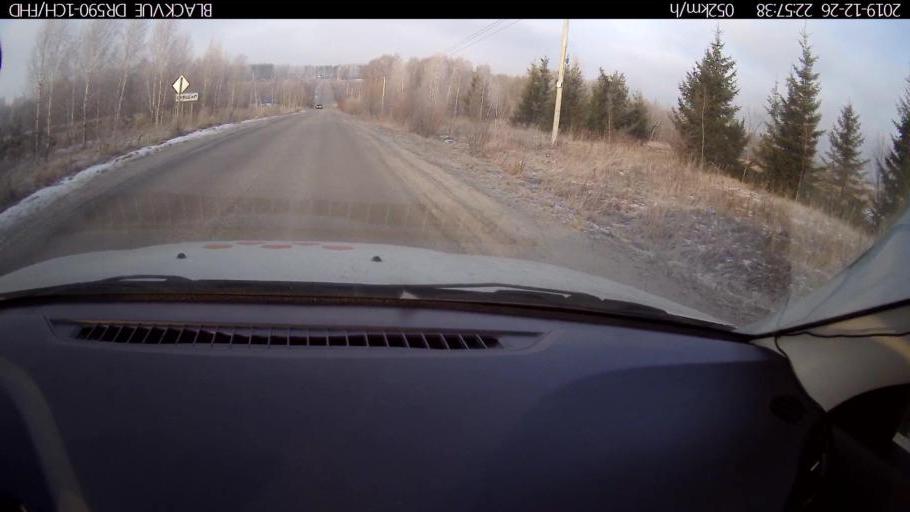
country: RU
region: Nizjnij Novgorod
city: Burevestnik
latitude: 56.1519
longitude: 43.7146
